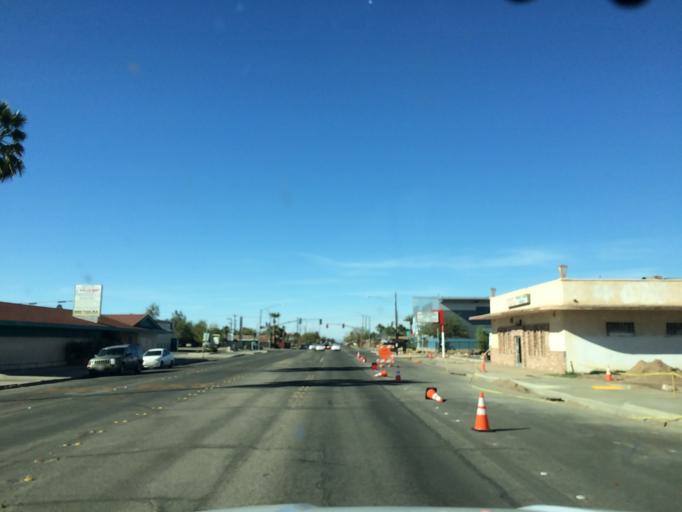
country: US
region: California
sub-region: Imperial County
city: El Centro
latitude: 32.7951
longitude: -115.5614
